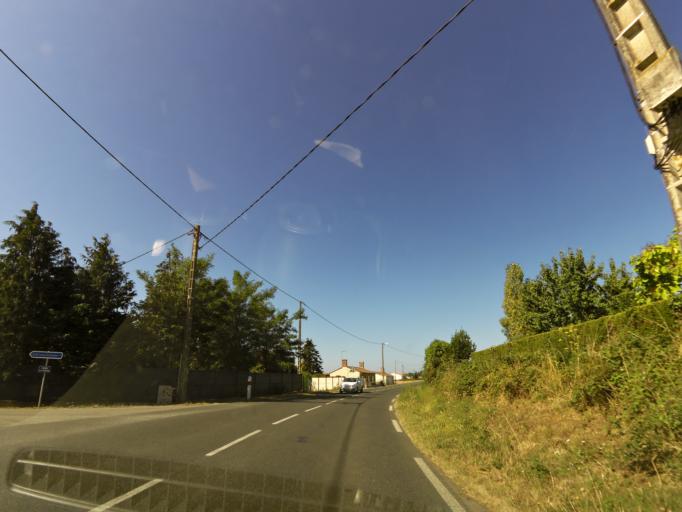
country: FR
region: Pays de la Loire
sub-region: Departement de la Vendee
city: Longeville-sur-Mer
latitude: 46.4216
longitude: -1.5178
